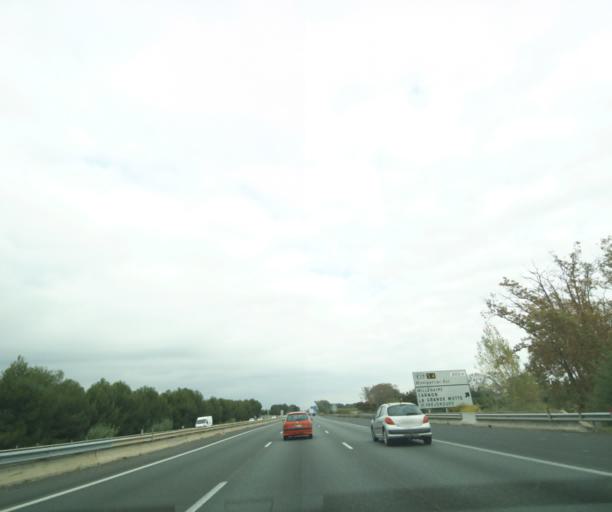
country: FR
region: Languedoc-Roussillon
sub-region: Departement de l'Herault
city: Lattes
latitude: 43.6014
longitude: 3.9214
